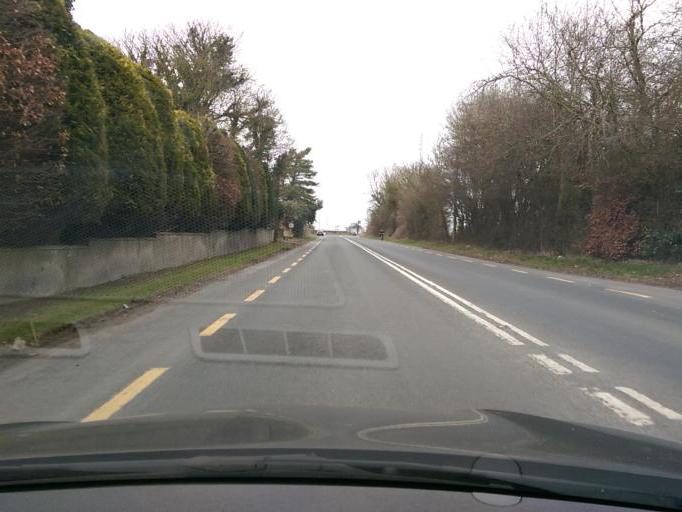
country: IE
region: Leinster
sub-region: An Iarmhi
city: Athlone
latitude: 53.3863
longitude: -7.9919
